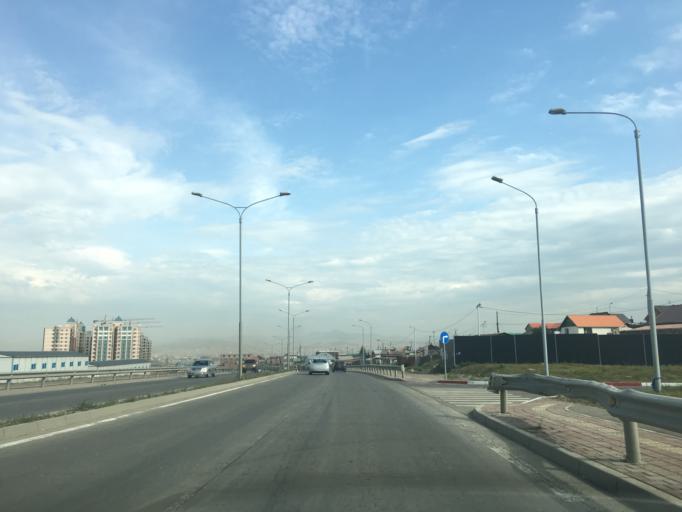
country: MN
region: Ulaanbaatar
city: Ulaanbaatar
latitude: 47.8632
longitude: 106.7884
